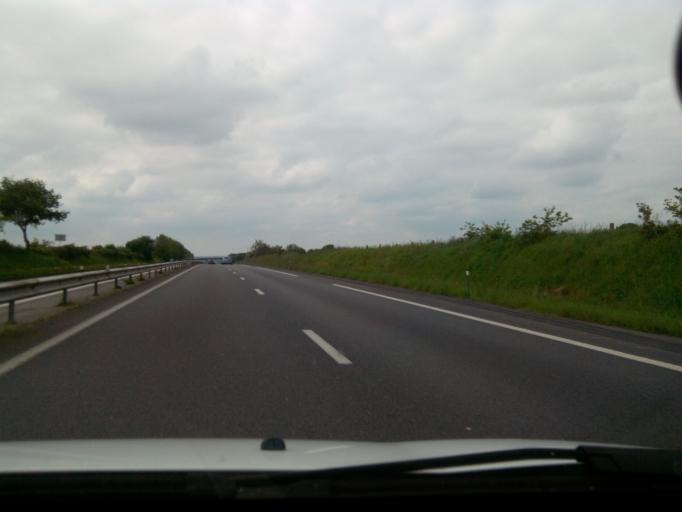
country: FR
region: Brittany
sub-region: Departement des Cotes-d'Armor
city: Caulnes
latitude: 48.2841
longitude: -2.1977
